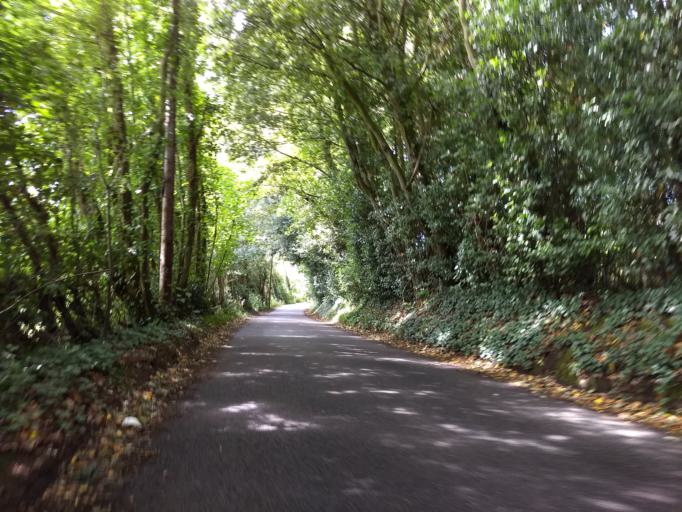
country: GB
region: England
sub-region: Isle of Wight
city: Newport
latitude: 50.6843
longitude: -1.2952
